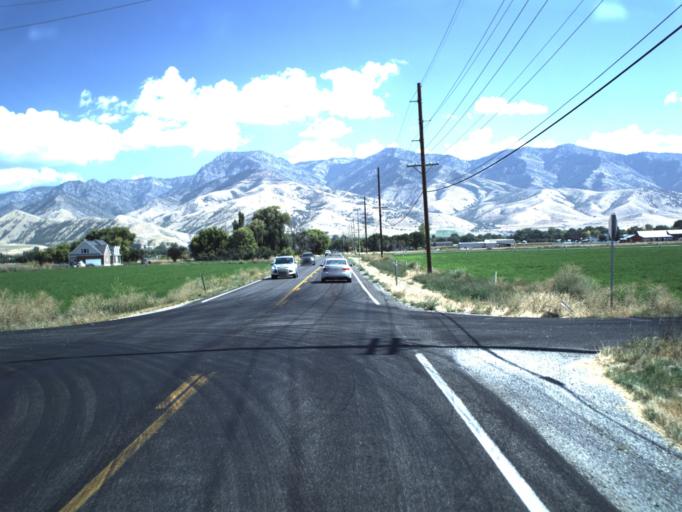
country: US
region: Utah
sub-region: Cache County
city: Smithfield
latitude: 41.8388
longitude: -111.8642
